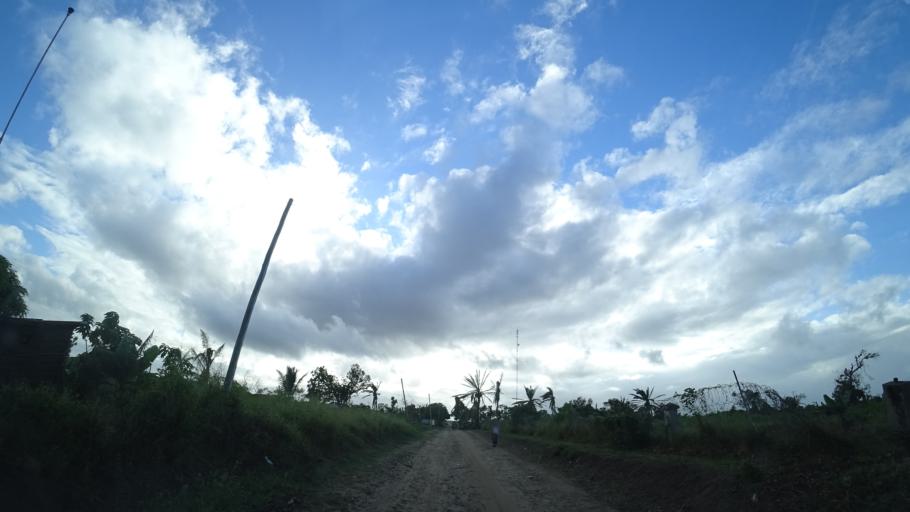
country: MZ
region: Sofala
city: Beira
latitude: -19.7145
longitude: 35.0100
